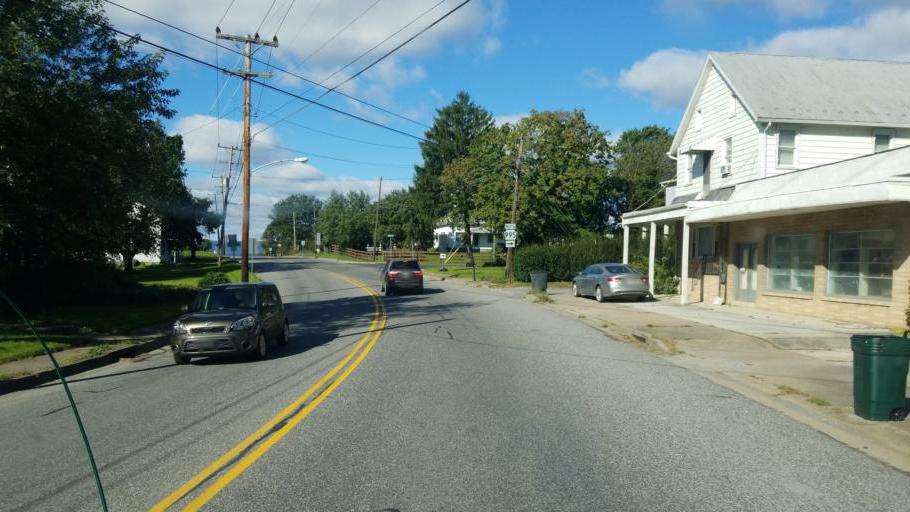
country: US
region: Pennsylvania
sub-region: Franklin County
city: Greencastle
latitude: 39.8053
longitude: -77.8069
